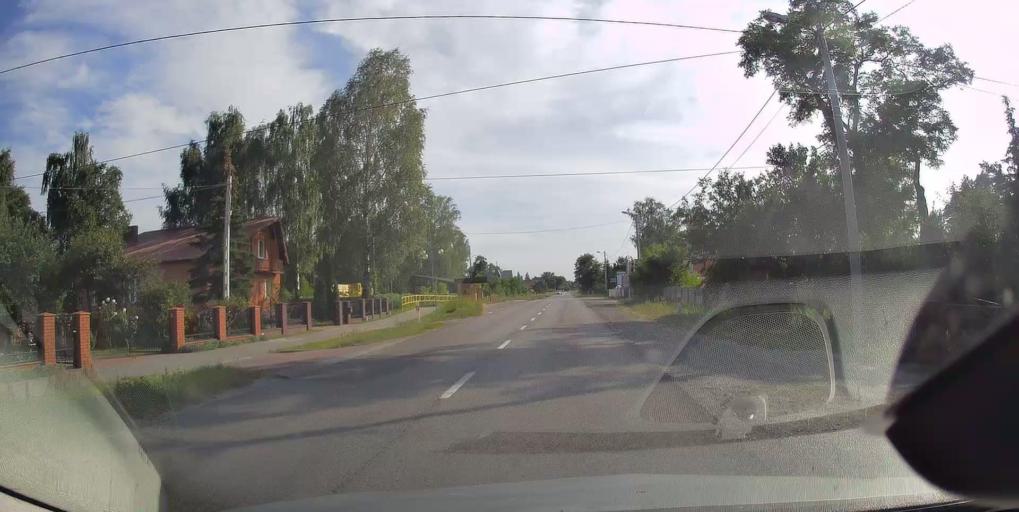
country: PL
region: Swietokrzyskie
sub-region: Powiat konecki
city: Radoszyce
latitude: 51.0782
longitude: 20.2819
